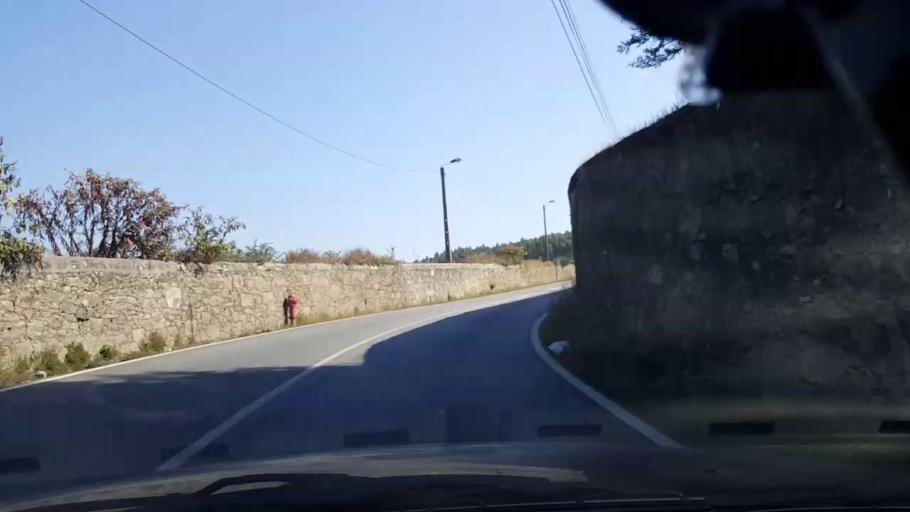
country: PT
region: Porto
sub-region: Vila do Conde
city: Arvore
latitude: 41.3637
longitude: -8.6730
